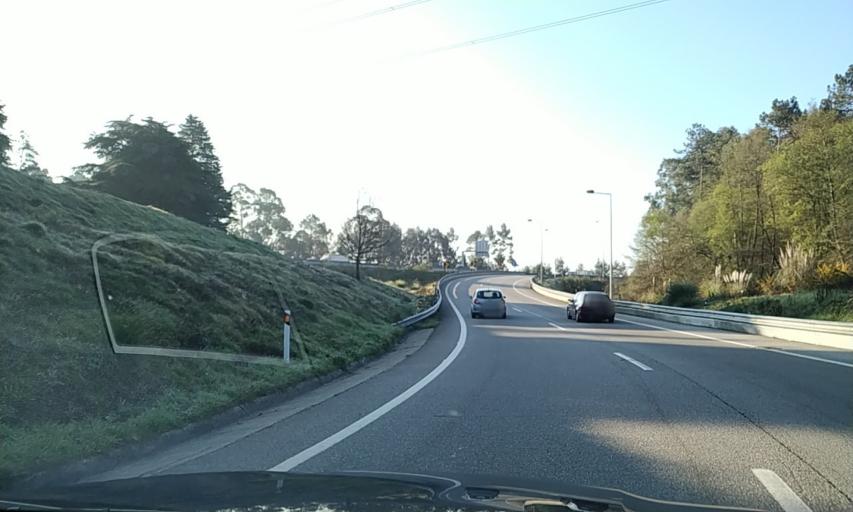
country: PT
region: Porto
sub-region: Valongo
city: Ermesinde
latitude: 41.2371
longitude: -8.5657
